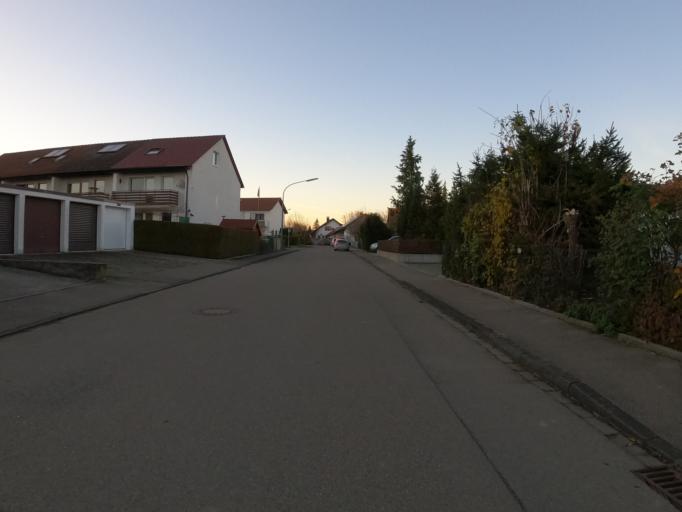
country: DE
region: Bavaria
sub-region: Swabia
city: Holzheim
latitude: 48.4171
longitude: 10.0742
